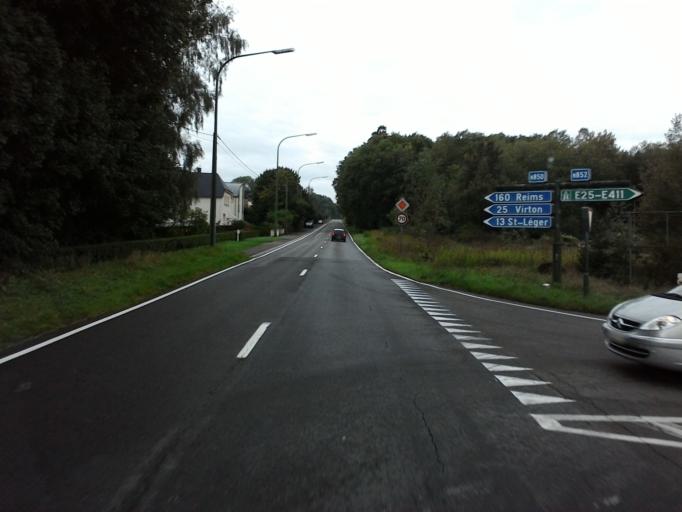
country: BE
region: Wallonia
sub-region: Province du Luxembourg
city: Arlon
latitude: 49.6734
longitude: 5.7902
